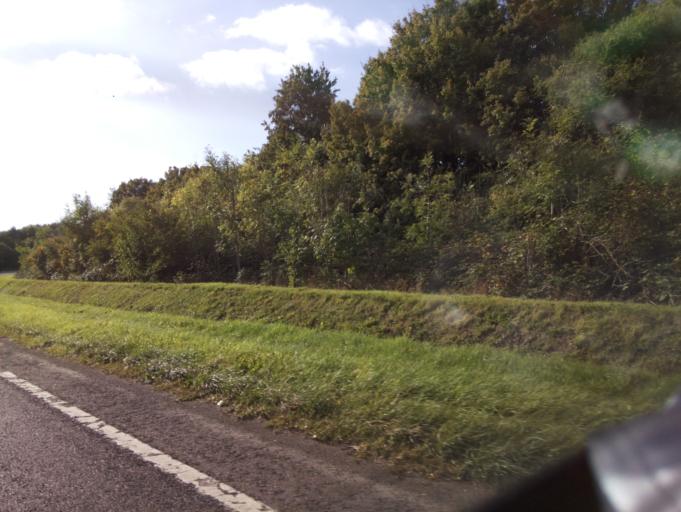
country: GB
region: England
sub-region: Hampshire
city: Basingstoke
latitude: 51.2544
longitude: -1.0966
